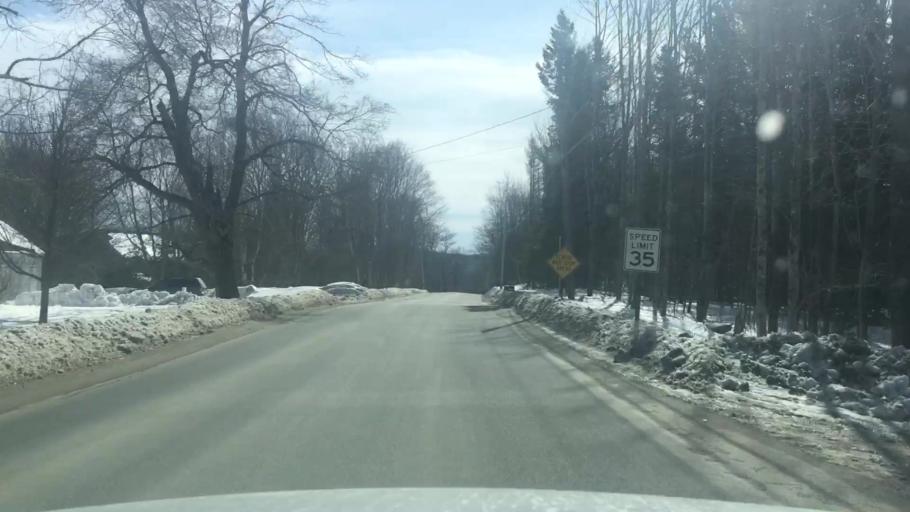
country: US
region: Maine
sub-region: Penobscot County
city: Holden
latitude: 44.7635
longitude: -68.6423
